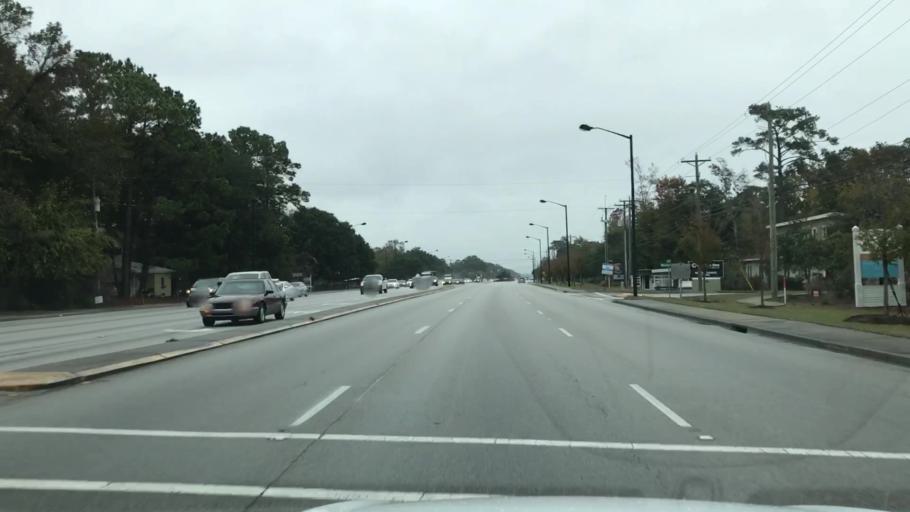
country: US
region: South Carolina
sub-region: Charleston County
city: Isle of Palms
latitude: 32.8544
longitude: -79.8015
